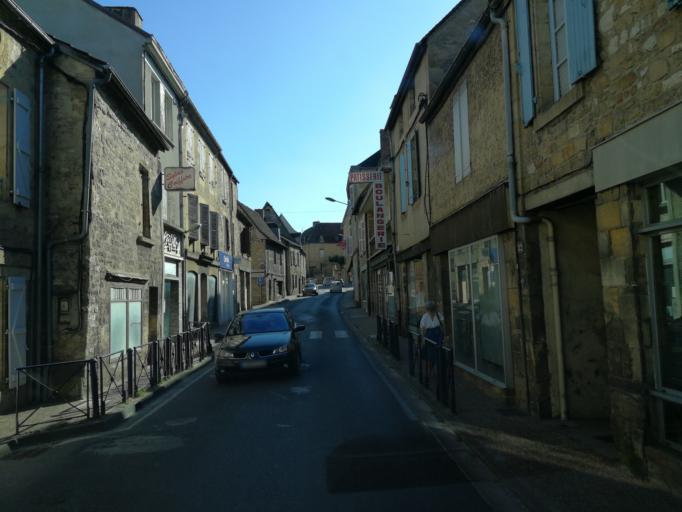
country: FR
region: Midi-Pyrenees
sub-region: Departement du Lot
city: Gourdon
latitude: 44.7352
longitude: 1.3794
